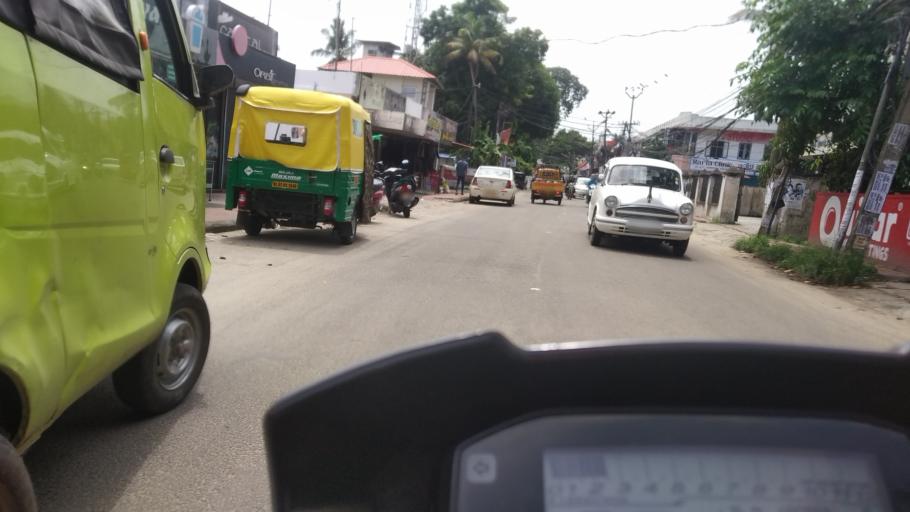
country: IN
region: Kerala
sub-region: Ernakulam
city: Cochin
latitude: 9.9916
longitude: 76.3091
